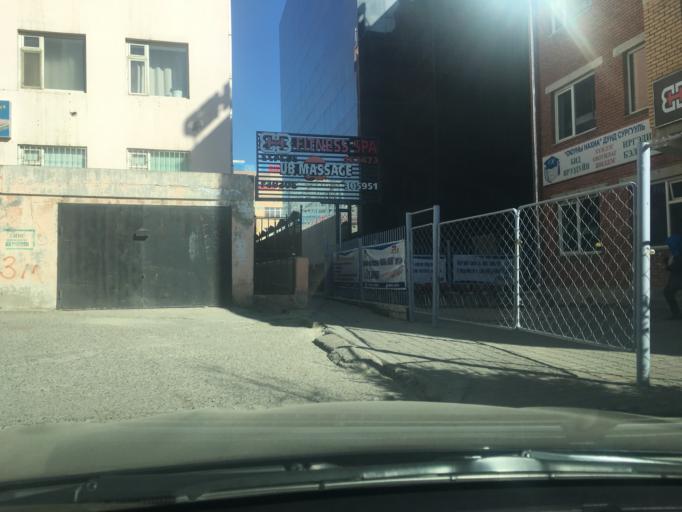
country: MN
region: Ulaanbaatar
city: Ulaanbaatar
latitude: 47.9224
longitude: 106.8883
